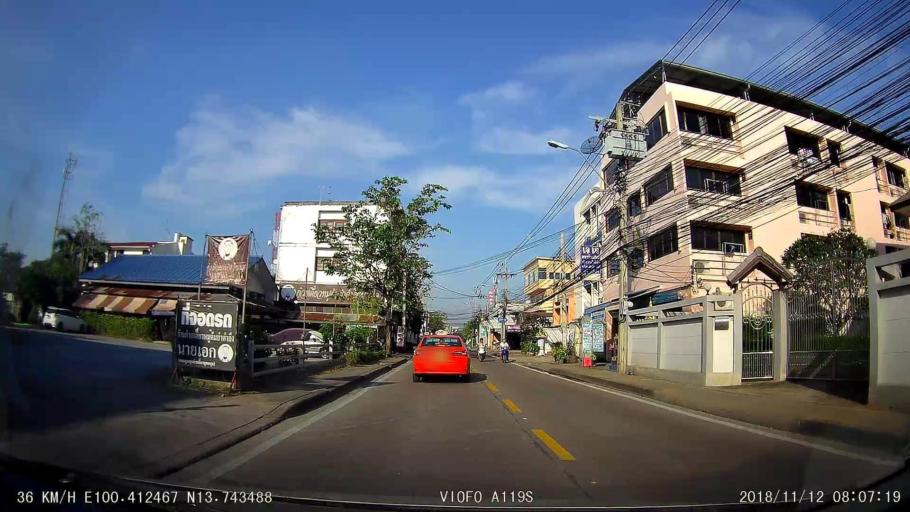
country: TH
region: Bangkok
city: Phasi Charoen
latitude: 13.7435
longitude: 100.4124
